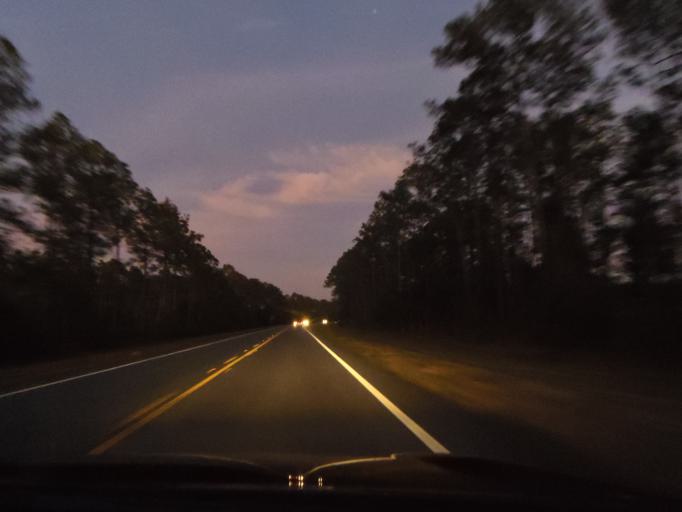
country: US
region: Florida
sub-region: Volusia County
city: De Leon Springs
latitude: 29.2396
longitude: -81.2542
